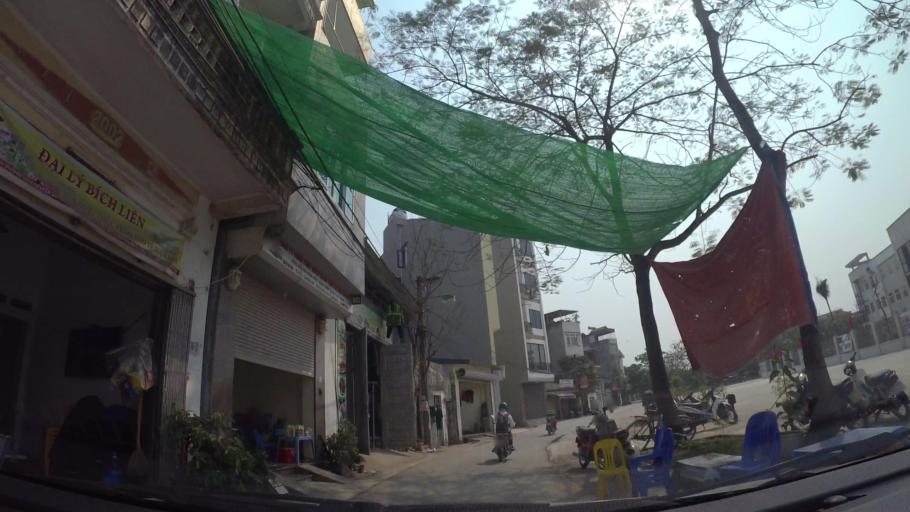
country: VN
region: Ha Noi
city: Ha Dong
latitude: 21.0018
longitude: 105.7580
